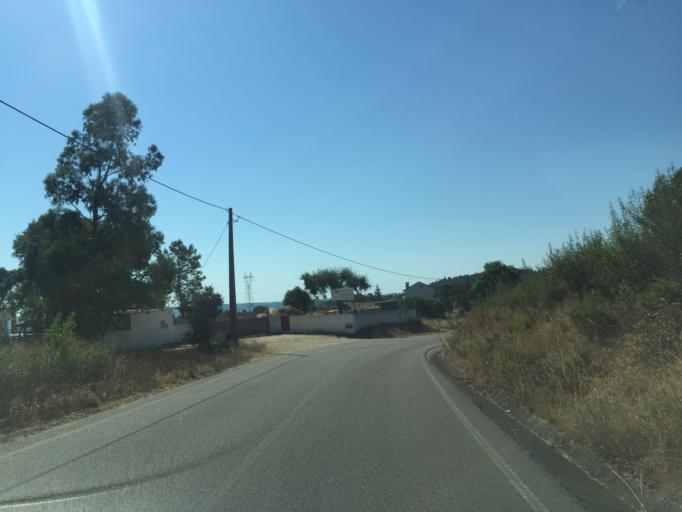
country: PT
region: Santarem
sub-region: Tomar
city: Tomar
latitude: 39.5802
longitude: -8.3260
